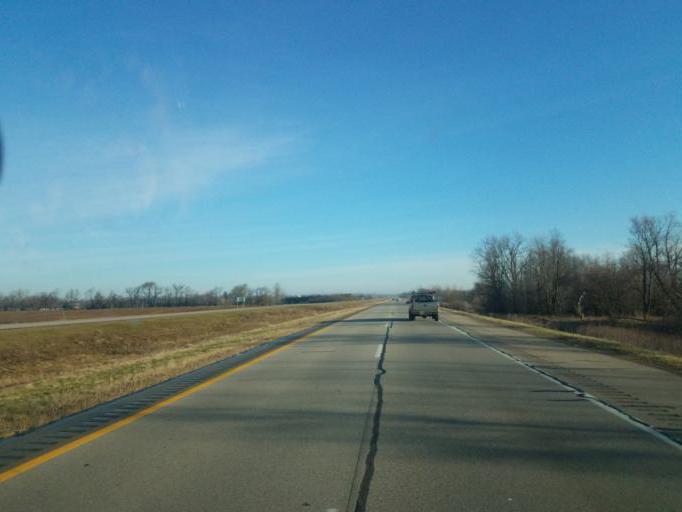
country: US
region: Michigan
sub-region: Clinton County
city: Saint Johns
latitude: 42.9441
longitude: -84.5184
